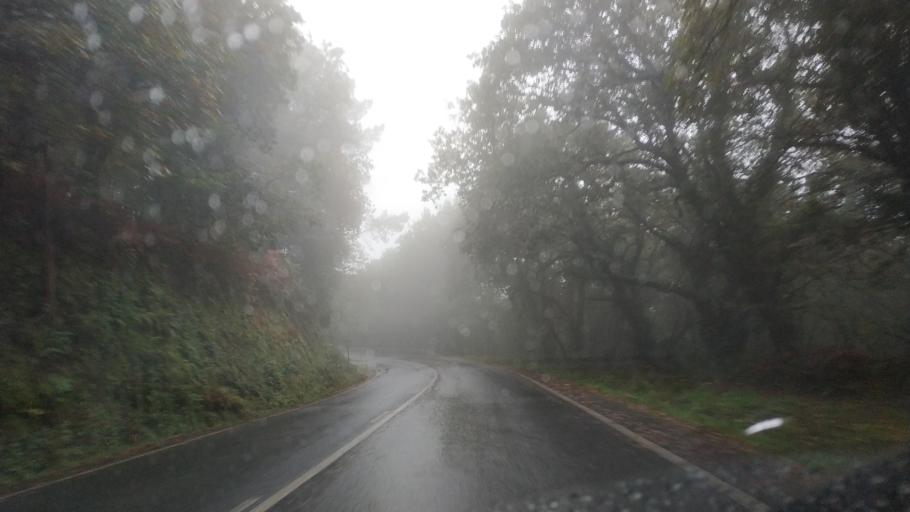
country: ES
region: Galicia
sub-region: Provincia da Coruna
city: Negreira
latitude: 42.9108
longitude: -8.7513
